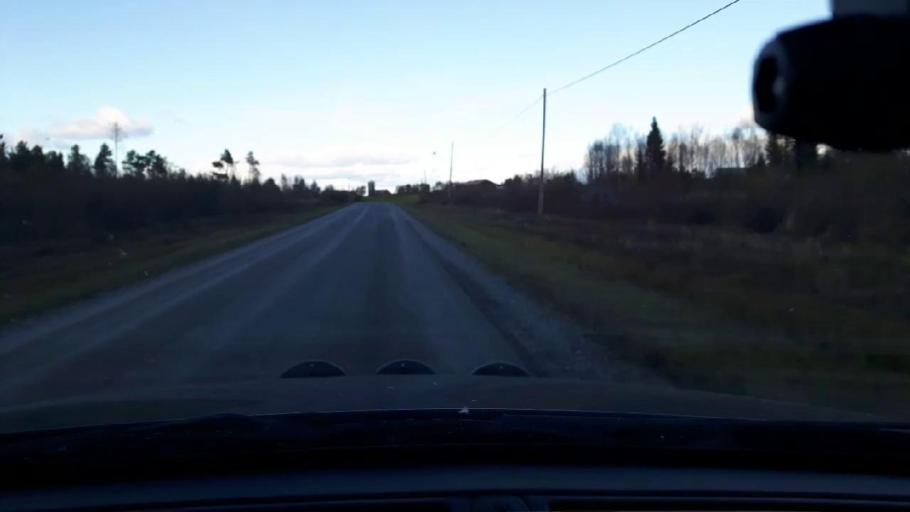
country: SE
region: Jaemtland
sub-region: Krokoms Kommun
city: Krokom
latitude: 63.0753
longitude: 14.2712
